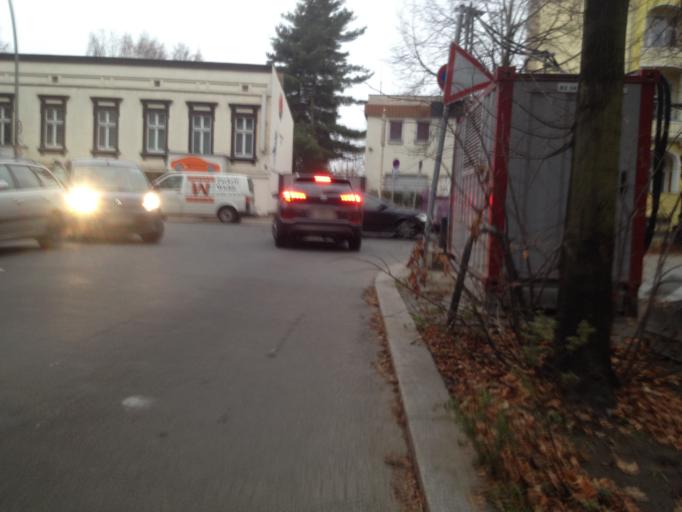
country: DE
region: Berlin
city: Heinersdorf
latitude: 52.5731
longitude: 13.4198
